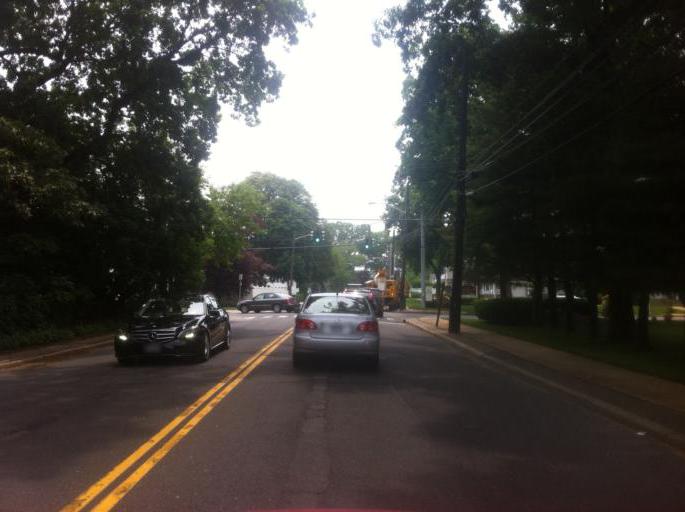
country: US
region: New York
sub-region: Nassau County
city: Massapequa
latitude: 40.6850
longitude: -73.4760
